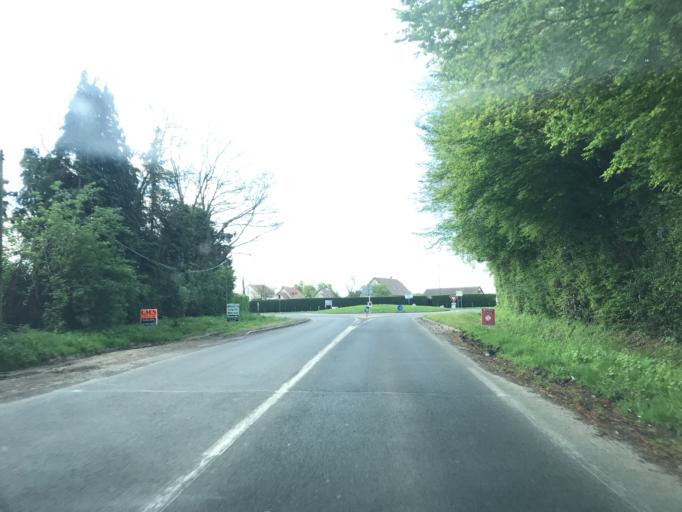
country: FR
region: Lower Normandy
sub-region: Departement du Calvados
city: Dozule
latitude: 49.2234
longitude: -0.0787
